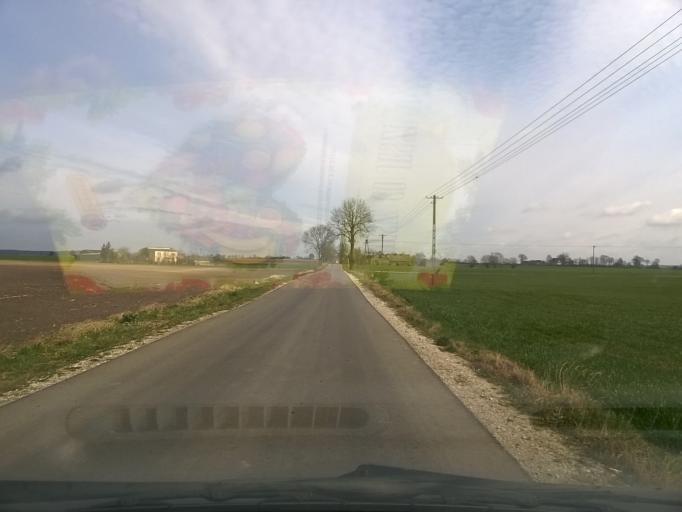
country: PL
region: Greater Poland Voivodeship
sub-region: Powiat wagrowiecki
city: Golancz
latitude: 52.9655
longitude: 17.3425
